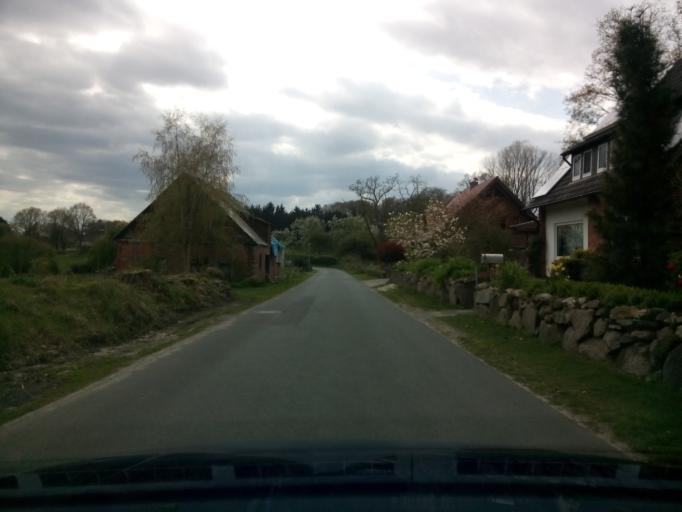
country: DE
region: Lower Saxony
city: Vollersode
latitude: 53.3208
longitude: 8.8896
